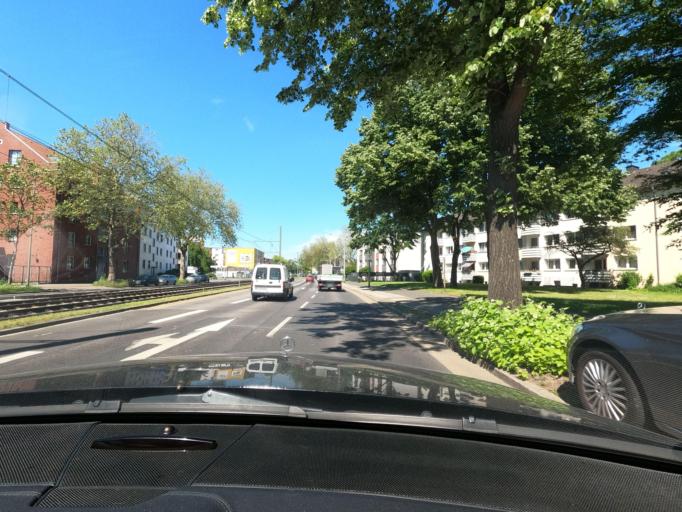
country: DE
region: North Rhine-Westphalia
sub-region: Regierungsbezirk Dusseldorf
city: Hochfeld
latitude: 51.4032
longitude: 6.7637
